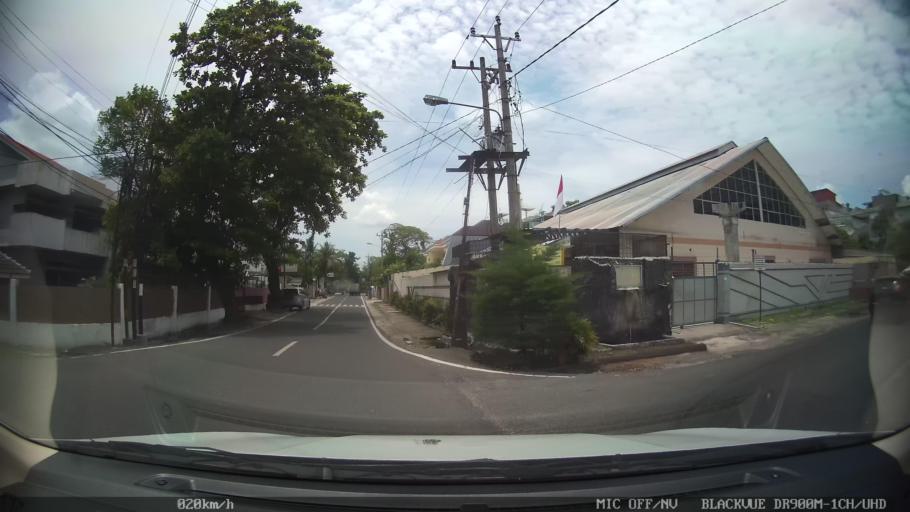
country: ID
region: North Sumatra
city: Medan
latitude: 3.5826
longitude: 98.6661
